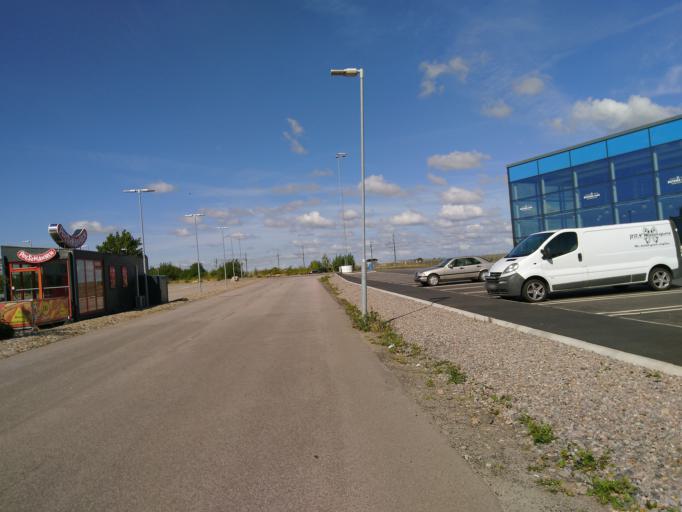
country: SE
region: Skane
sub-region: Landskrona
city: Landskrona
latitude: 55.8737
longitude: 12.8595
